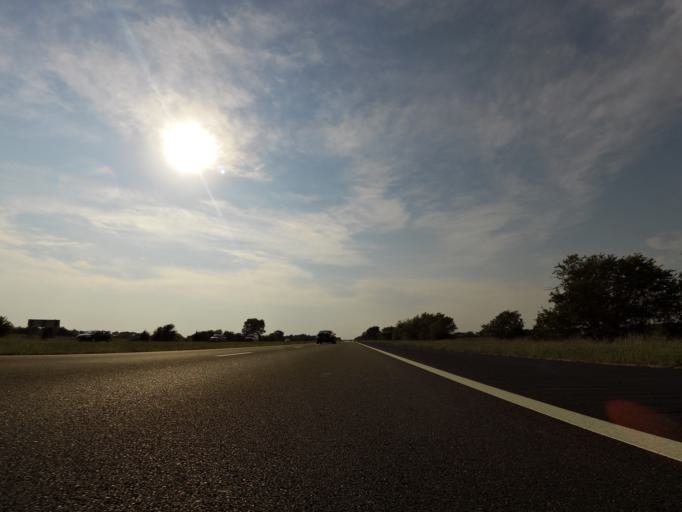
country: US
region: Kansas
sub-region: Reno County
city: Haven
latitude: 37.8823
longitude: -97.7210
